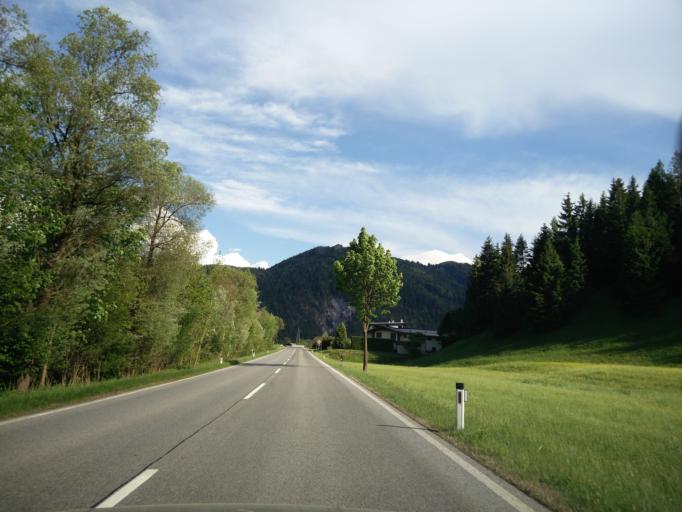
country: AT
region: Tyrol
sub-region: Politischer Bezirk Kitzbuhel
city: Kirchdorf in Tirol
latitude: 47.5854
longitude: 12.4721
